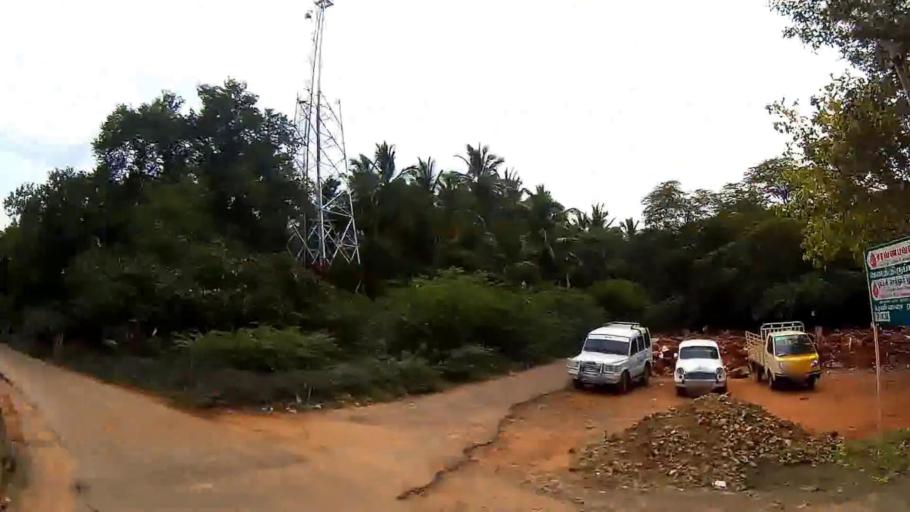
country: VN
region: Lao Cai
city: Sa Pa
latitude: 22.3346
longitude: 103.8415
